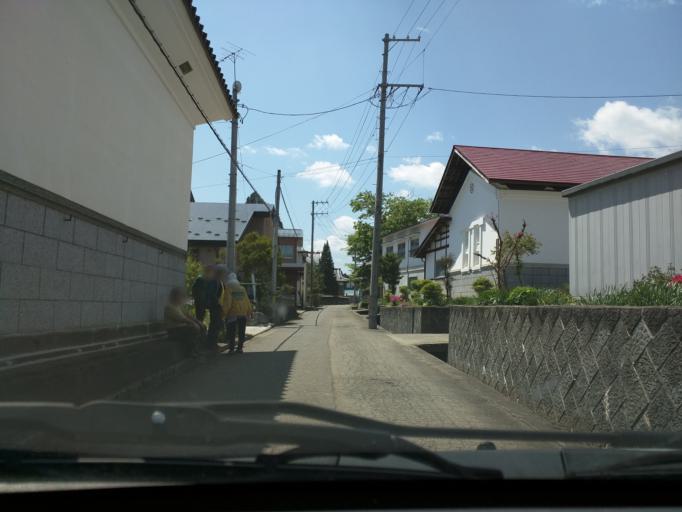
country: JP
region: Fukushima
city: Kitakata
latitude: 37.6392
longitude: 139.8373
